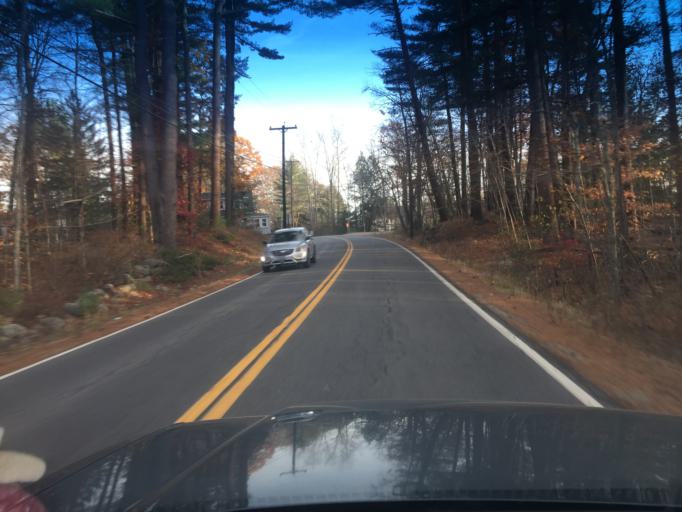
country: US
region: Maine
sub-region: York County
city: Eliot
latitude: 43.1866
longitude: -70.7450
